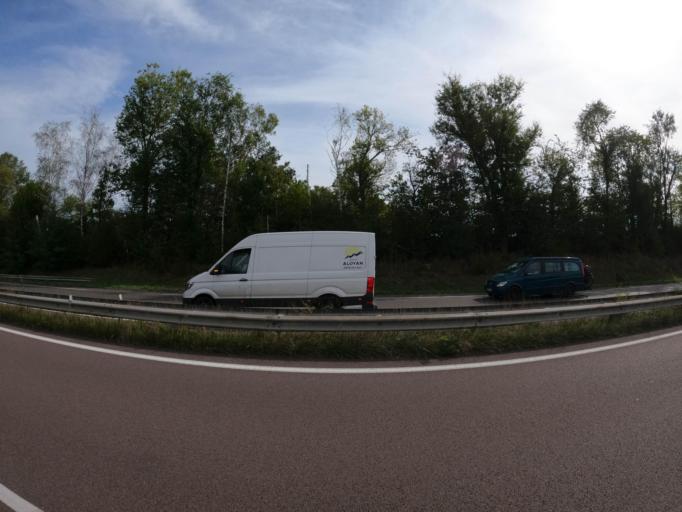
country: FR
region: Bourgogne
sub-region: Departement de Saone-et-Loire
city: Sanvignes-les-Mines
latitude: 46.6488
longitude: 4.3291
